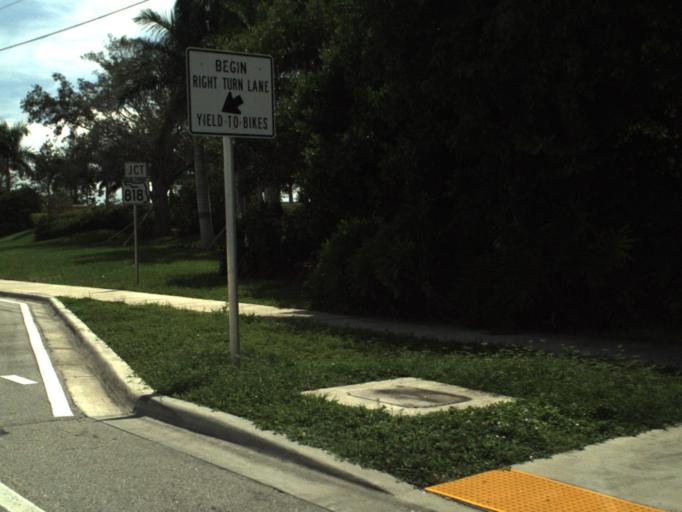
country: US
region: Florida
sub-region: Broward County
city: Davie
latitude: 26.0694
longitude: -80.2525
